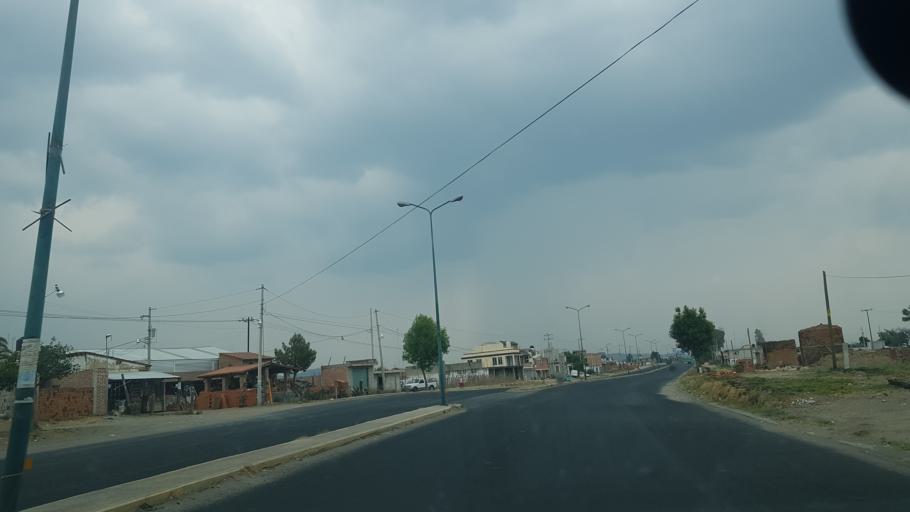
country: MX
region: Puebla
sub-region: Huejotzingo
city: San Mateo Capultitlan
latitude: 19.1781
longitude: -98.4156
